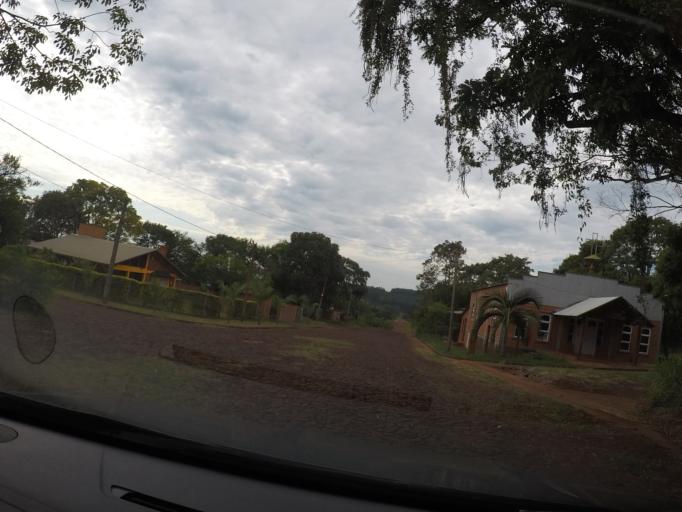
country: AR
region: Misiones
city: Puerto Rico
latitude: -26.8110
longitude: -55.0138
